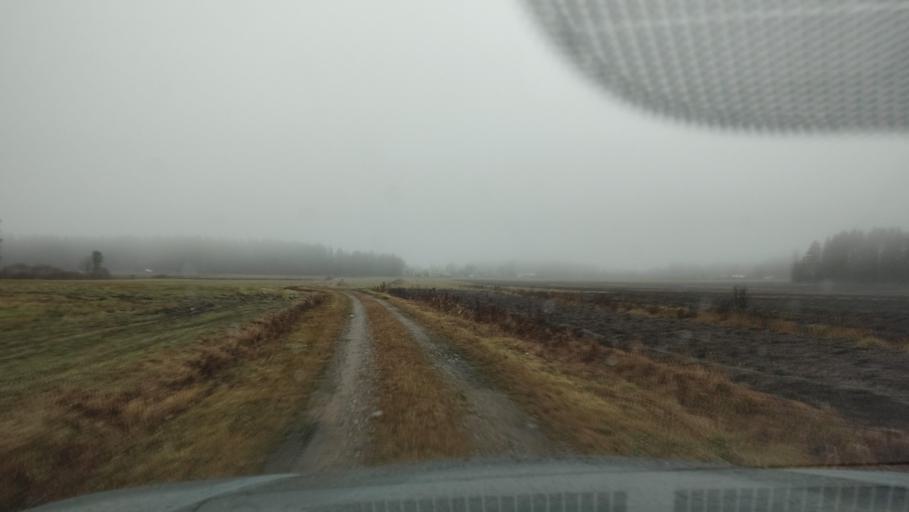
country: FI
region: Southern Ostrobothnia
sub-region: Suupohja
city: Karijoki
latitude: 62.1884
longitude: 21.7860
